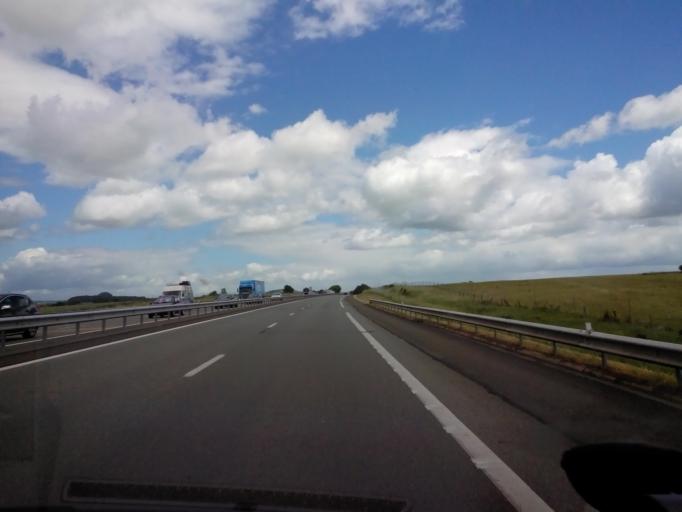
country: FR
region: Champagne-Ardenne
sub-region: Departement de la Haute-Marne
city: Avrecourt
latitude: 48.0207
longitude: 5.5314
